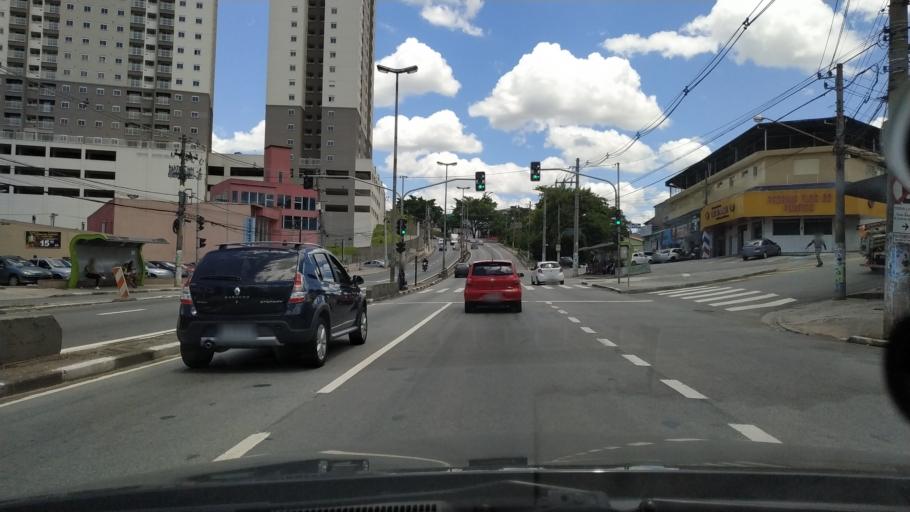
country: BR
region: Sao Paulo
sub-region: Barueri
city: Barueri
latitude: -23.4980
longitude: -46.8768
